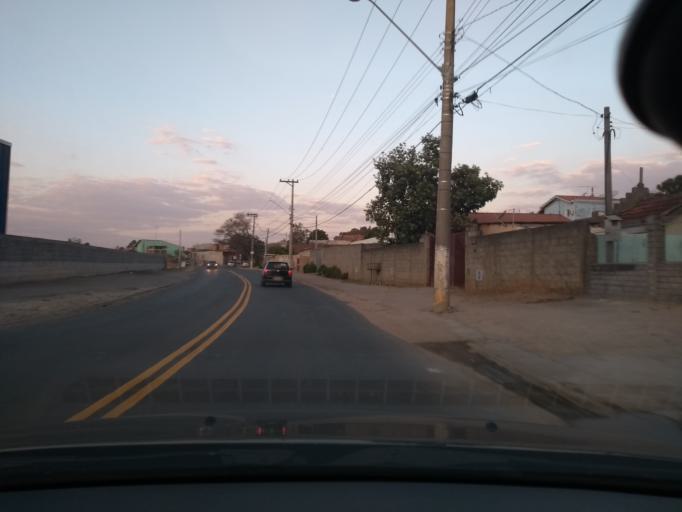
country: BR
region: Sao Paulo
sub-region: Itupeva
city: Itupeva
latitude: -23.1429
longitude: -47.0385
